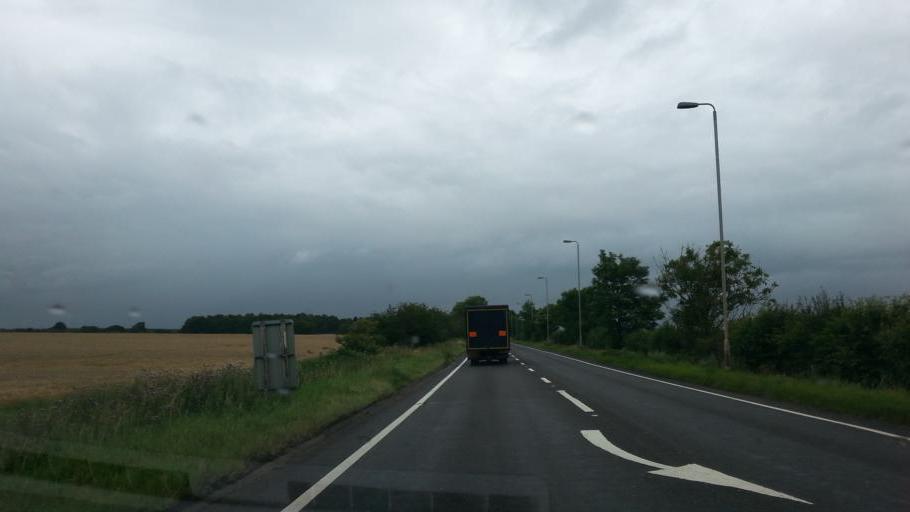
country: GB
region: England
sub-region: Nottinghamshire
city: Bilsthorpe
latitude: 53.1444
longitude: -1.0481
